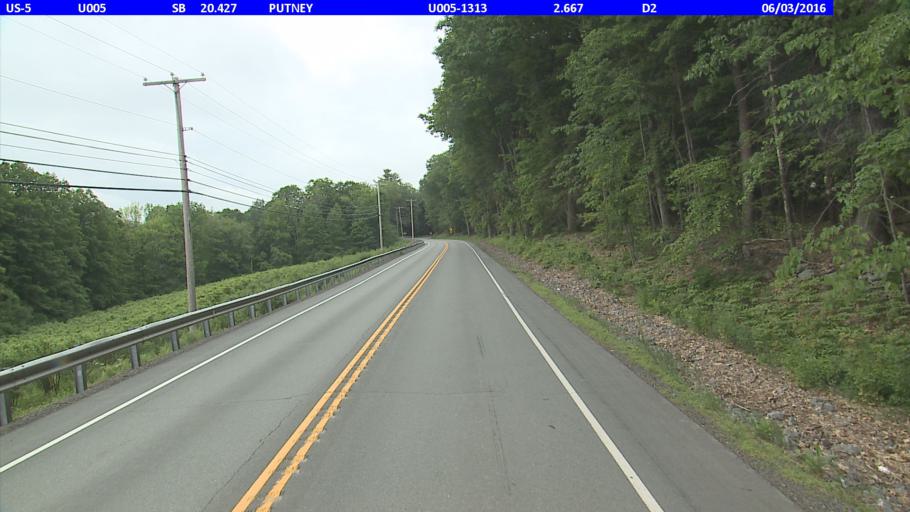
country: US
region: New Hampshire
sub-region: Cheshire County
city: Westmoreland
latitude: 42.9955
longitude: -72.4959
